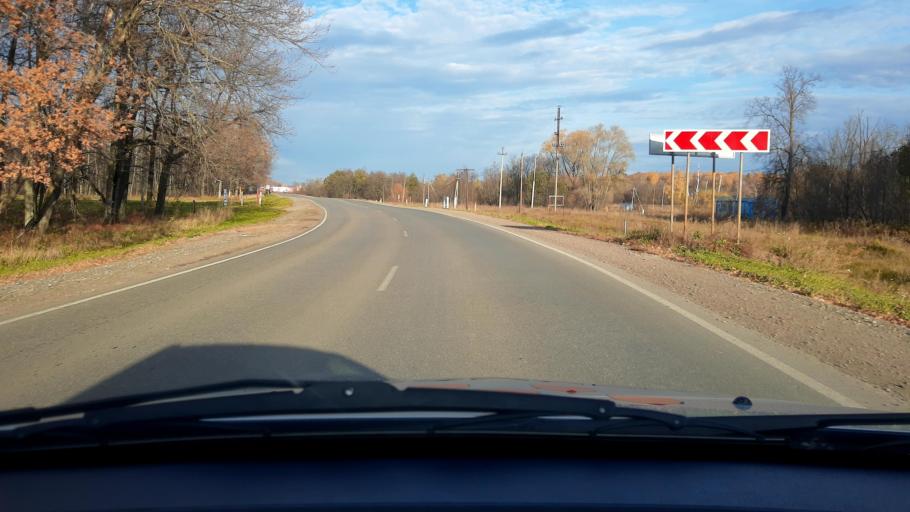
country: RU
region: Bashkortostan
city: Mikhaylovka
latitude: 54.8063
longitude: 55.8223
